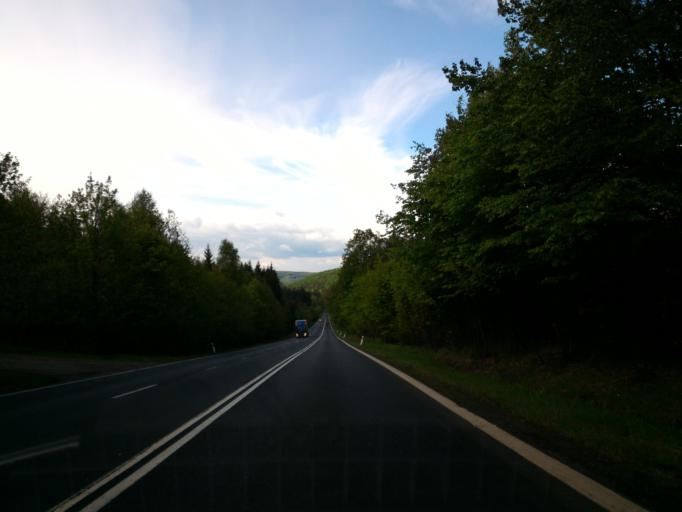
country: CZ
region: Ustecky
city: Dolni Podluzi
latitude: 50.8455
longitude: 14.5908
